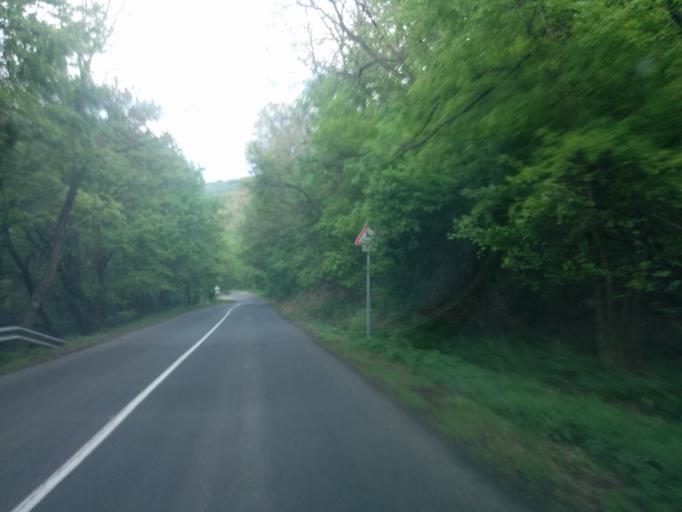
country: HU
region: Nograd
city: Romhany
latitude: 47.8839
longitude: 19.2314
